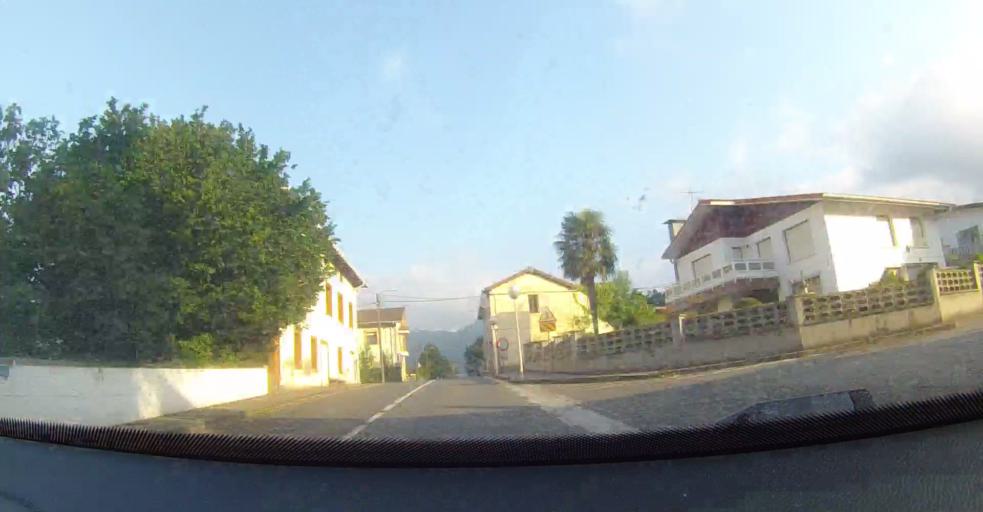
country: ES
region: Basque Country
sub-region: Bizkaia
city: Sopuerta
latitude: 43.2728
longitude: -3.1559
